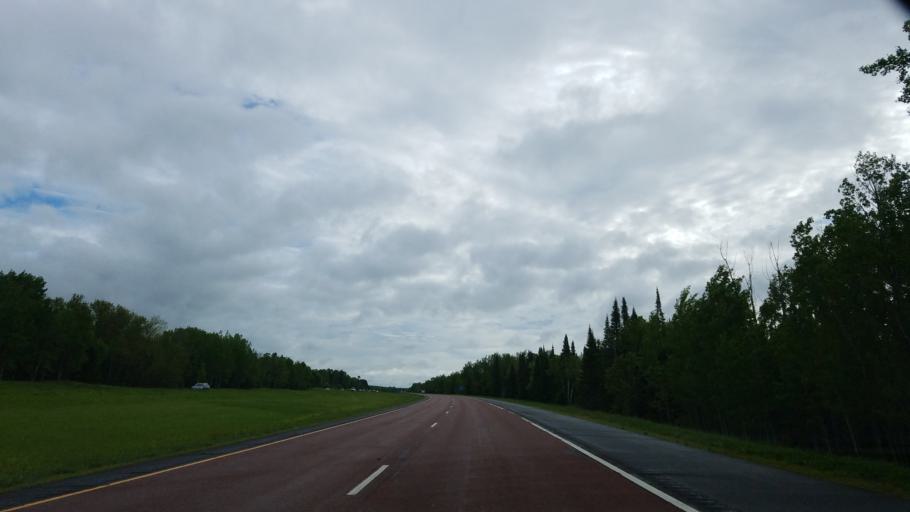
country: US
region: Minnesota
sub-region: Saint Louis County
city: Arnold
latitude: 46.8953
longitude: -91.9079
